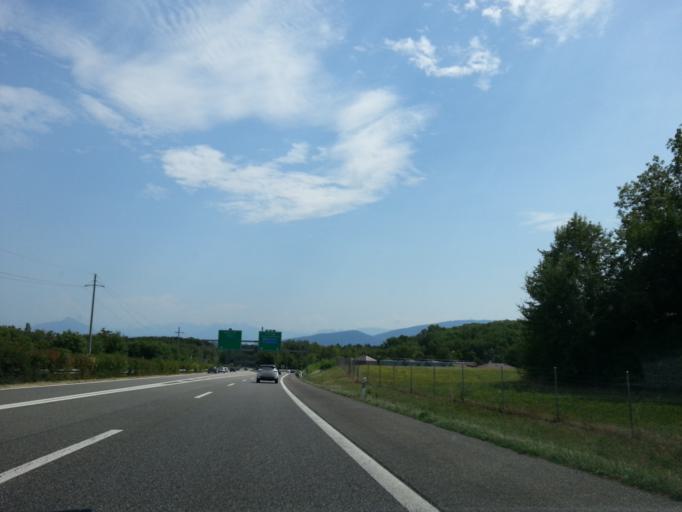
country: CH
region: Geneva
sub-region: Geneva
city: Bellevue
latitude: 46.2556
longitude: 6.1366
